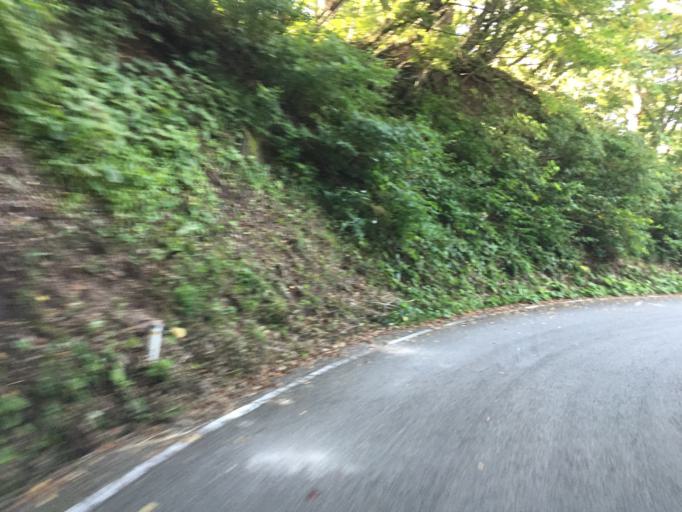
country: JP
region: Fukushima
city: Inawashiro
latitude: 37.4817
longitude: 139.9770
